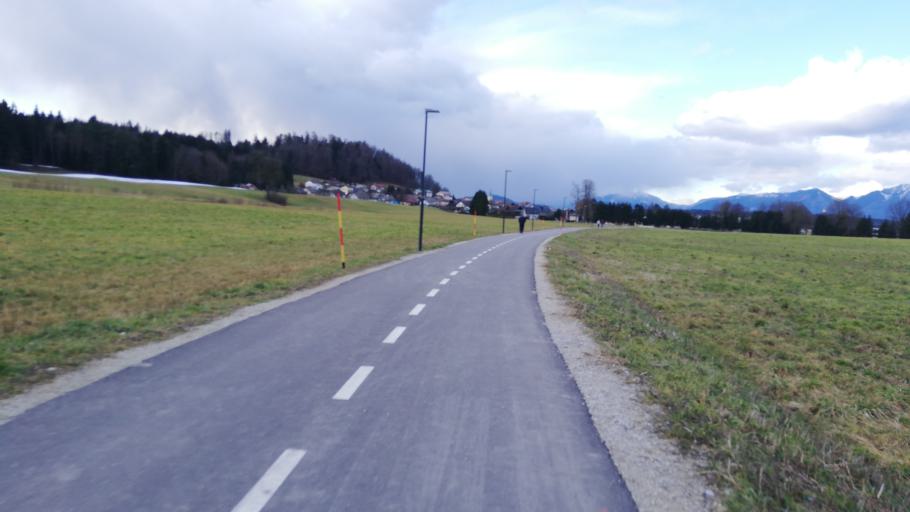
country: SI
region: Medvode
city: Medvode
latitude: 46.1261
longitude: 14.4169
